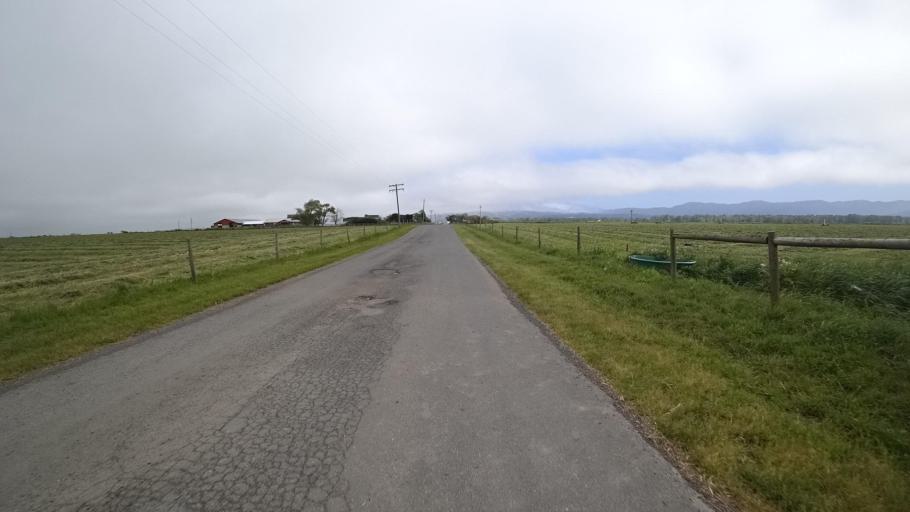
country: US
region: California
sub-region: Humboldt County
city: Fortuna
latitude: 40.5660
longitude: -124.1878
